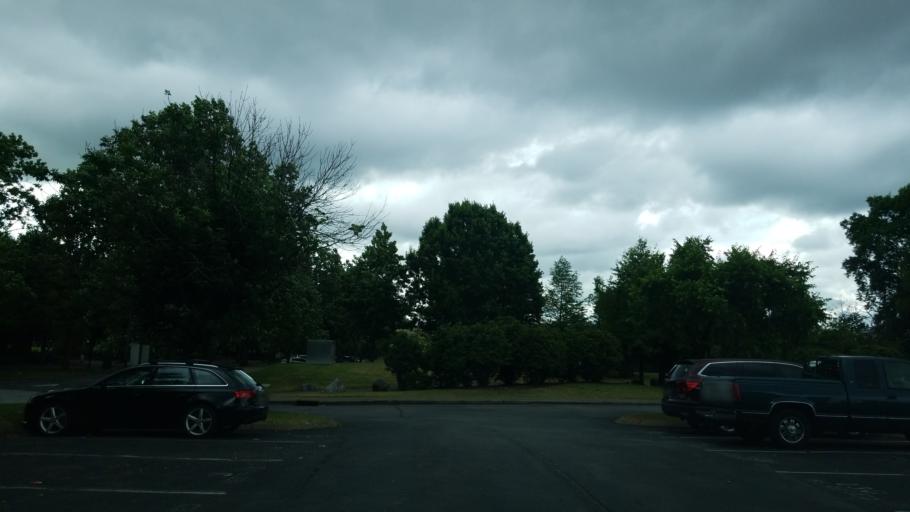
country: US
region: Tennessee
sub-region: Davidson County
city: Nashville
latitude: 36.1700
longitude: -86.7859
